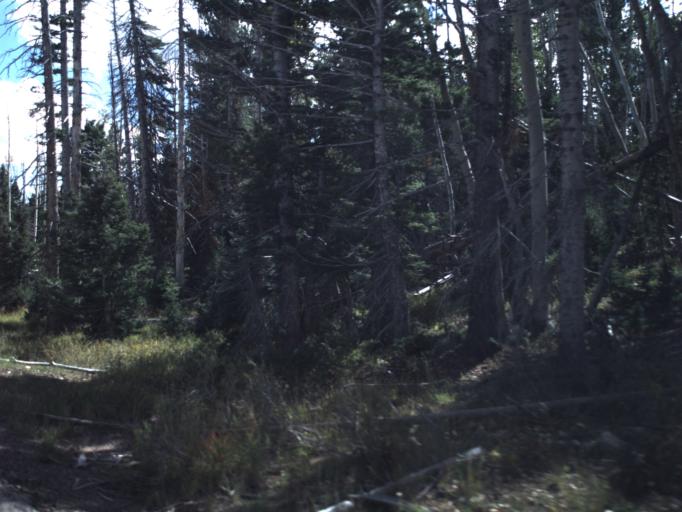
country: US
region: Utah
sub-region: Iron County
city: Parowan
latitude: 37.5299
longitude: -112.7652
